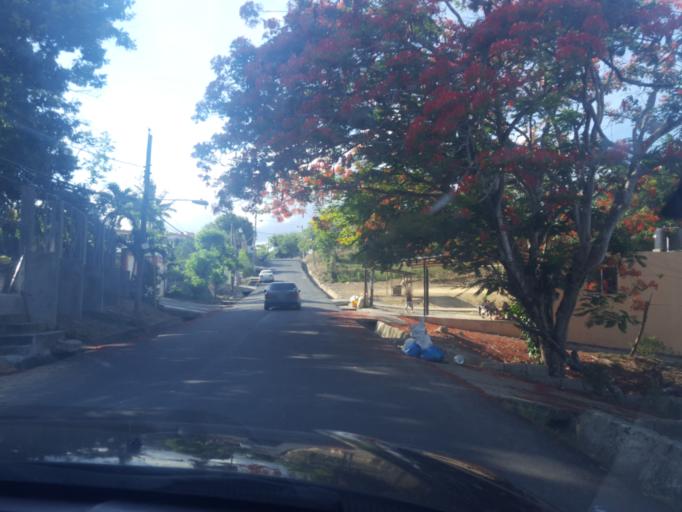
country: DO
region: La Vega
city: Rio Verde Arriba
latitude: 19.3490
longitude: -70.6260
